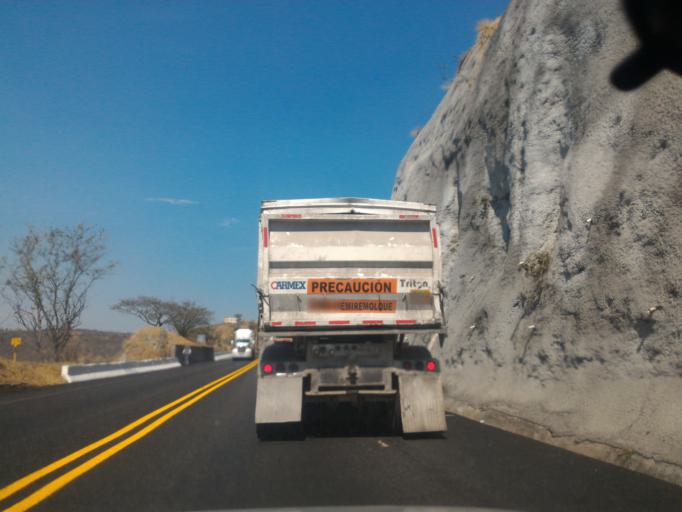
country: MX
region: Jalisco
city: Tuxpan
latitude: 19.5226
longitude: -103.4336
